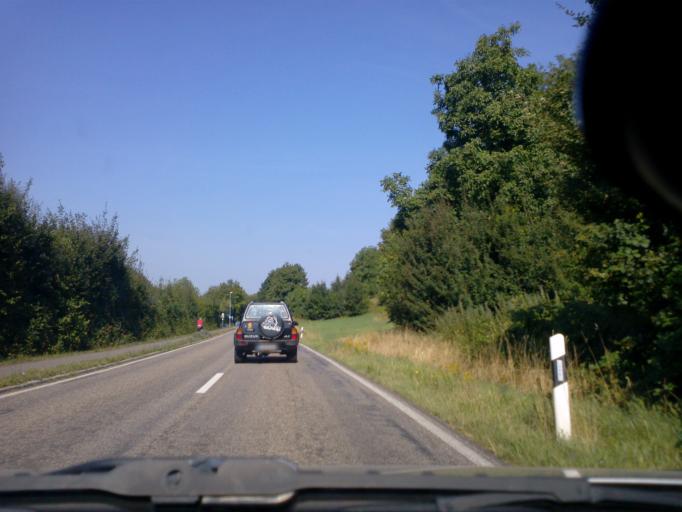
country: DE
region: Baden-Wuerttemberg
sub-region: Karlsruhe Region
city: Weingarten
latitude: 49.0818
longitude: 8.5660
